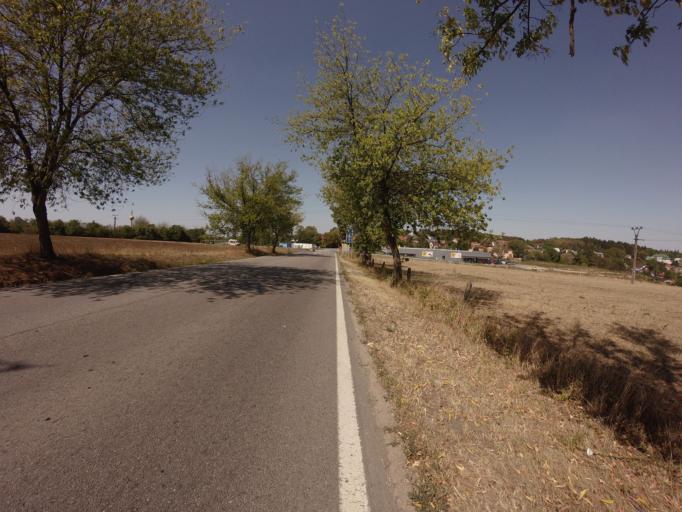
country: CZ
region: Central Bohemia
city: Jilove u Prahy
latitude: 49.9050
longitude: 14.4943
